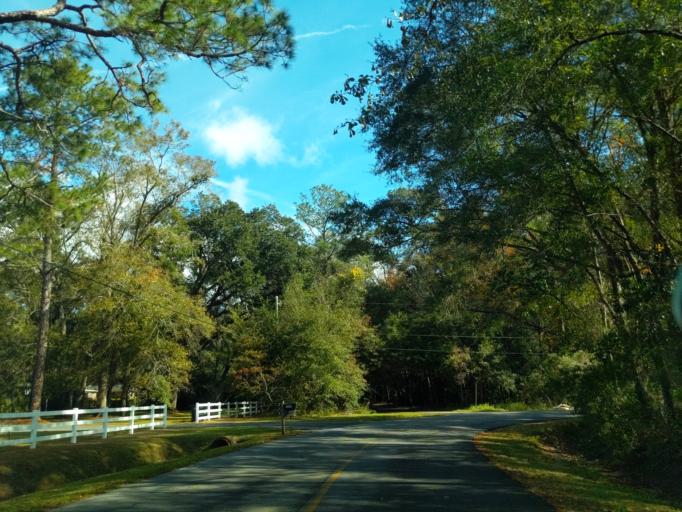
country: US
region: Florida
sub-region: Leon County
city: Tallahassee
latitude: 30.4740
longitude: -84.2063
